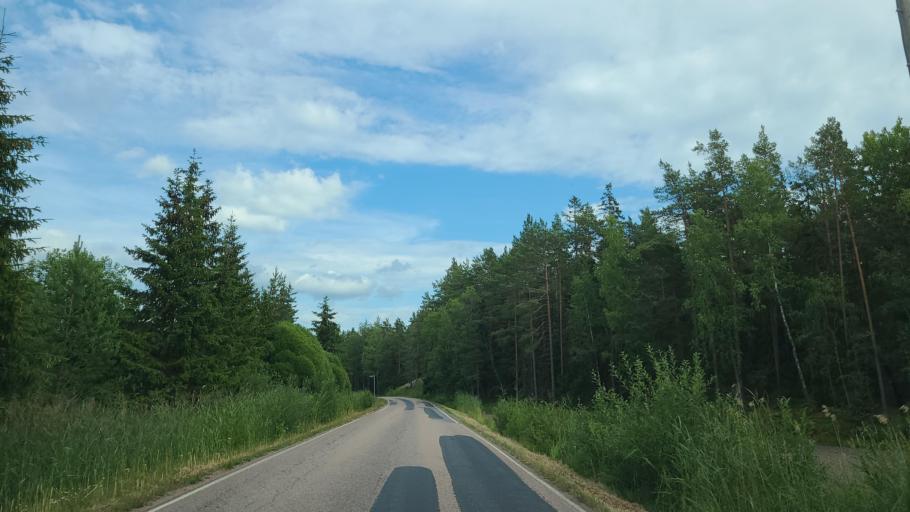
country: FI
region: Varsinais-Suomi
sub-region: Turku
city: Rymaettylae
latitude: 60.3457
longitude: 21.9700
